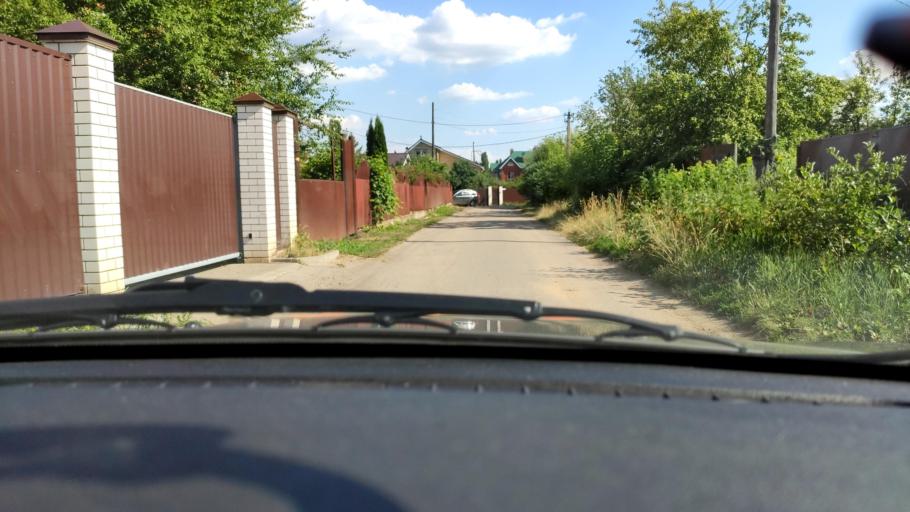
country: RU
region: Voronezj
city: Ramon'
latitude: 51.8302
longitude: 39.2683
